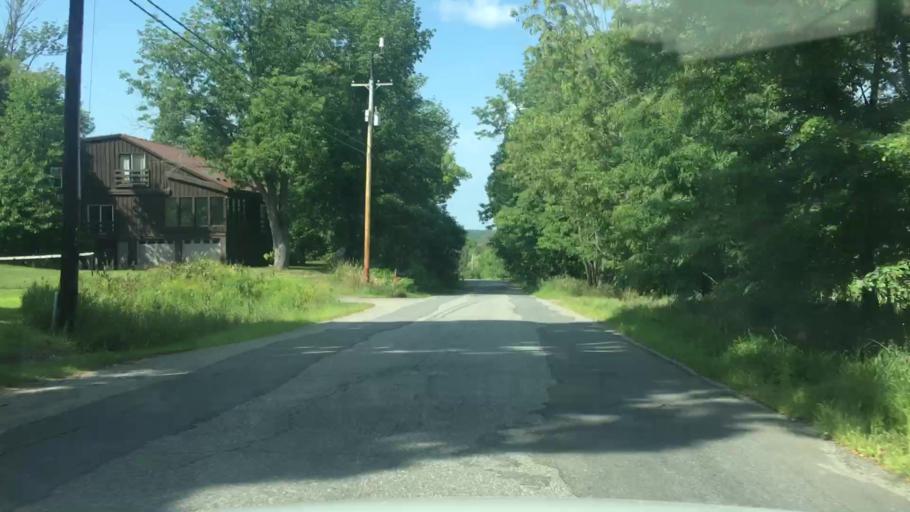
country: US
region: Maine
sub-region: Kennebec County
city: Waterville
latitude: 44.5731
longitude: -69.6667
